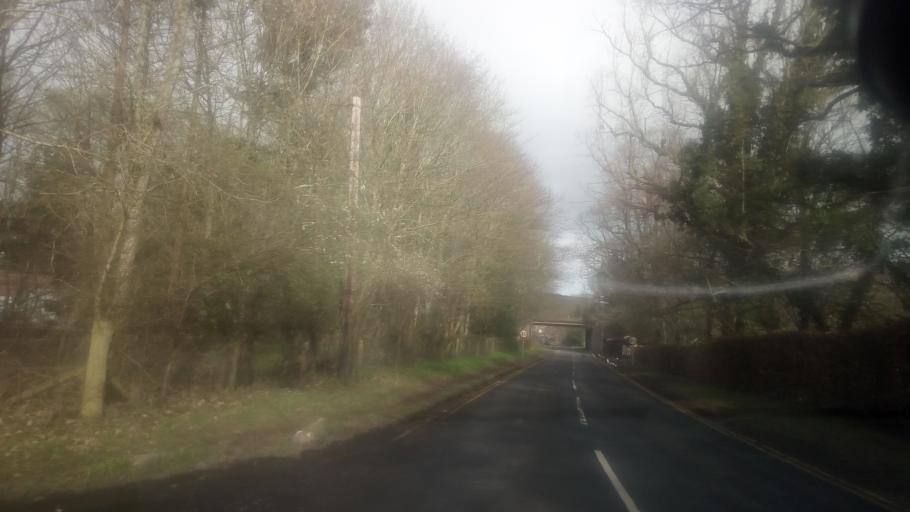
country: GB
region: Scotland
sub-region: The Scottish Borders
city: Melrose
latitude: 55.5956
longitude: -2.7387
